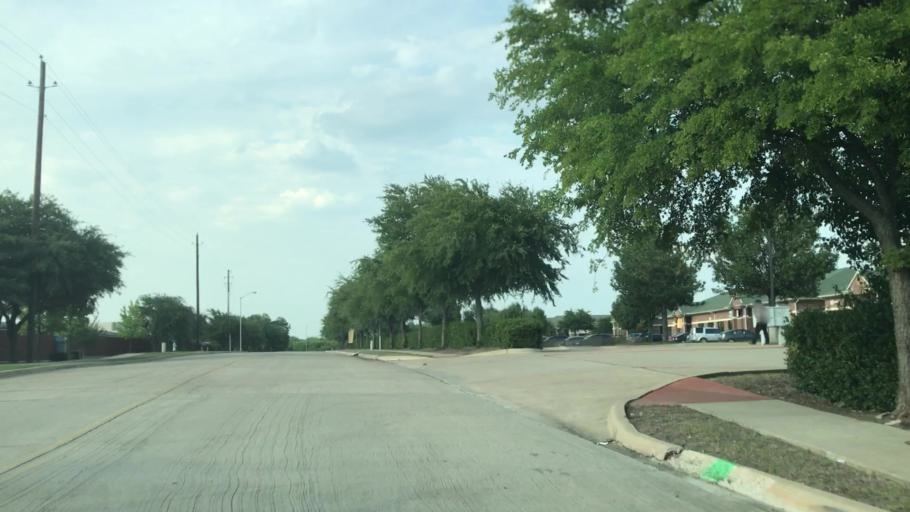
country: US
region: Texas
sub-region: Rockwall County
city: Rockwall
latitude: 32.9164
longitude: -96.4543
